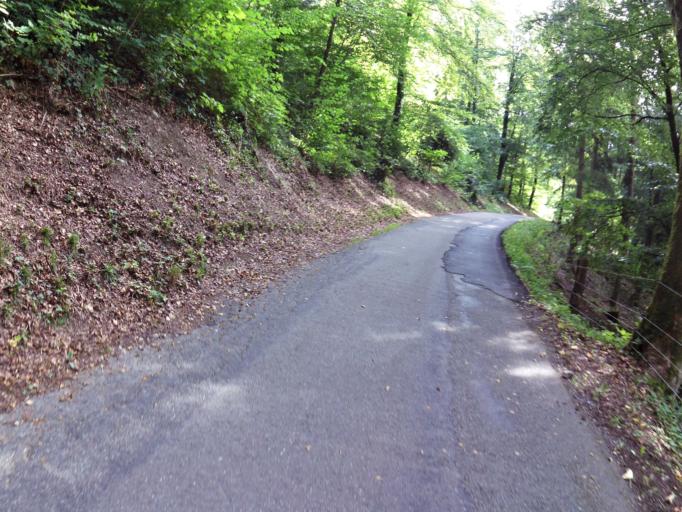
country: DE
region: Baden-Wuerttemberg
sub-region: Freiburg Region
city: Oberndorf
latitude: 48.3254
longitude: 8.5928
